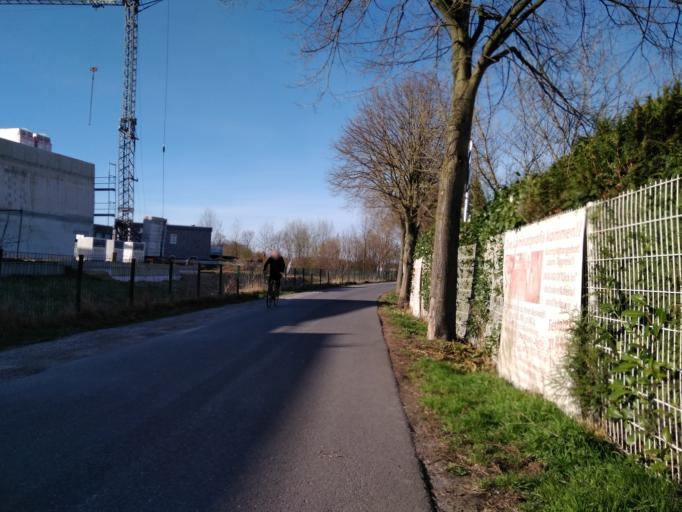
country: DE
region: North Rhine-Westphalia
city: Dorsten
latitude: 51.6115
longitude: 6.9237
